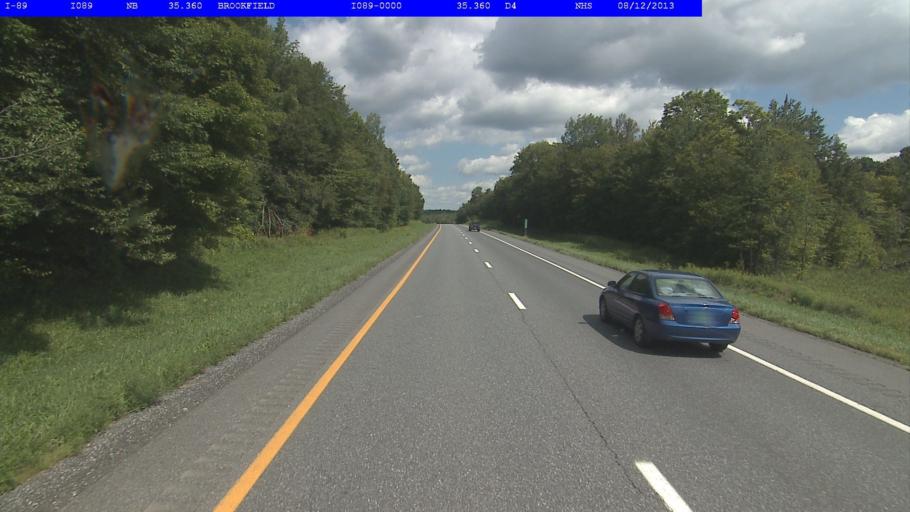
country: US
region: Vermont
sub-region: Orange County
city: Randolph
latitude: 44.0083
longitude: -72.6193
